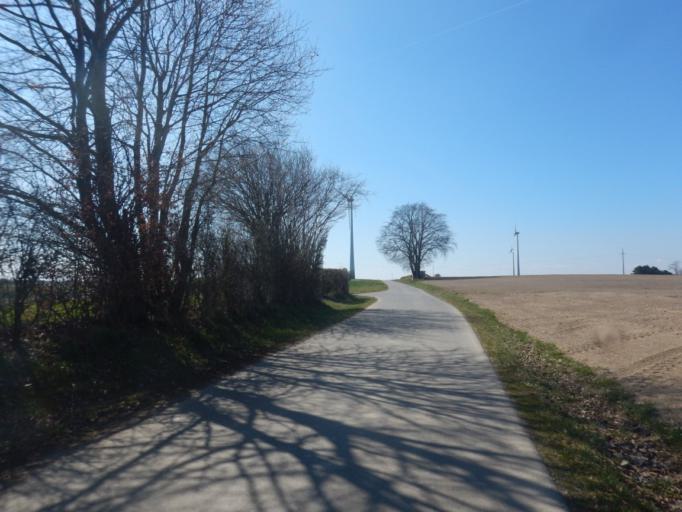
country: LU
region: Diekirch
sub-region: Canton de Clervaux
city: Troisvierges
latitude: 50.1126
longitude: 6.0314
